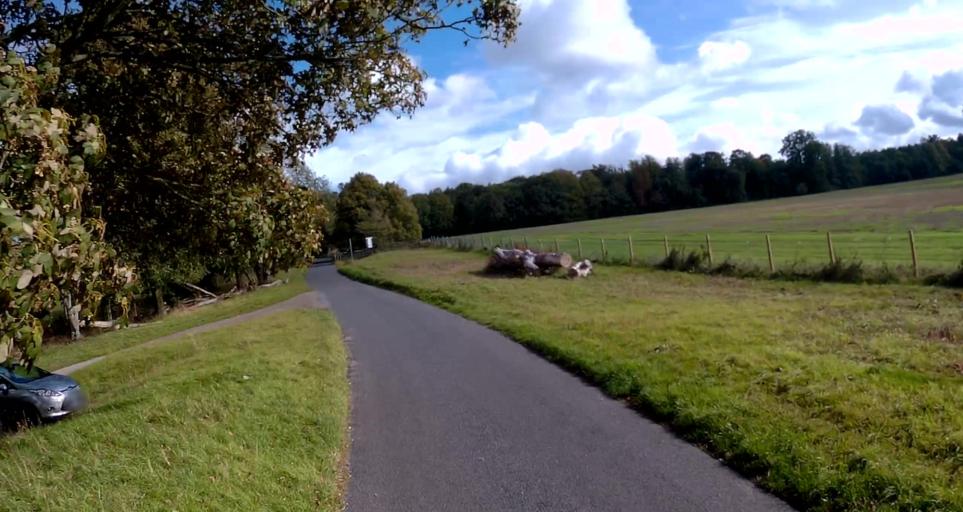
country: GB
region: England
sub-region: Hampshire
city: Kings Worthy
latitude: 51.0854
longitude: -1.2473
